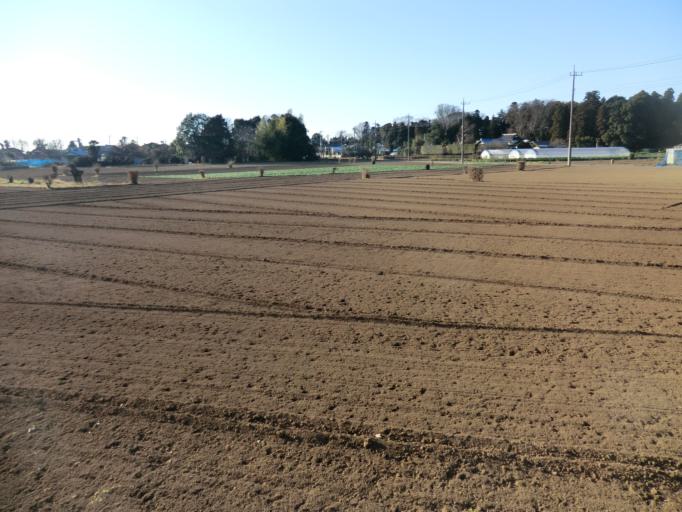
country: JP
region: Ibaraki
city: Mitsukaido
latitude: 35.9733
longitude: 139.9522
